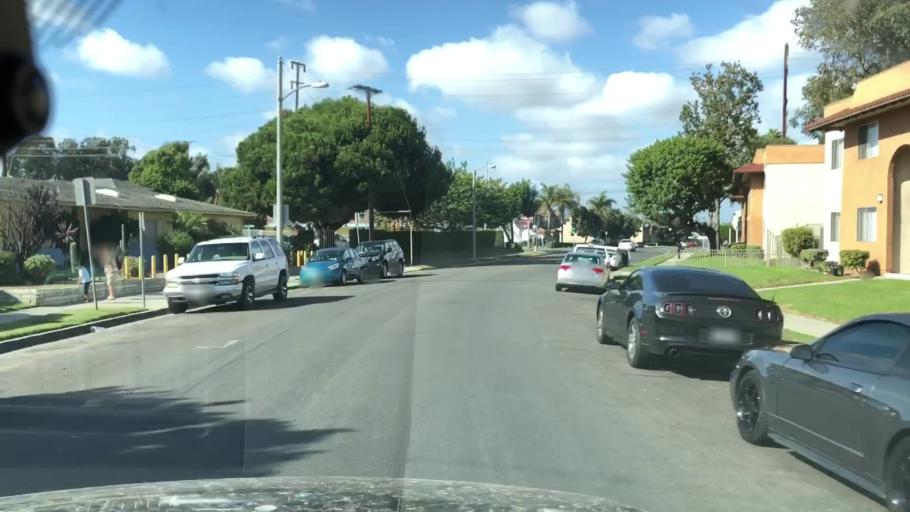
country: US
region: California
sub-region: Ventura County
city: Oxnard
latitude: 34.1724
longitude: -119.1675
